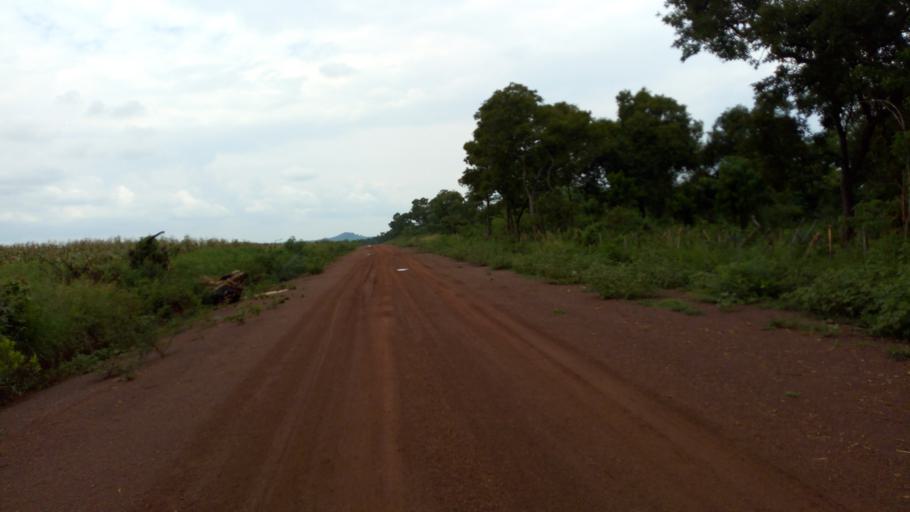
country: UG
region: Western Region
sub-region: Masindi District
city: Masindi
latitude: 1.5468
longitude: 31.7478
